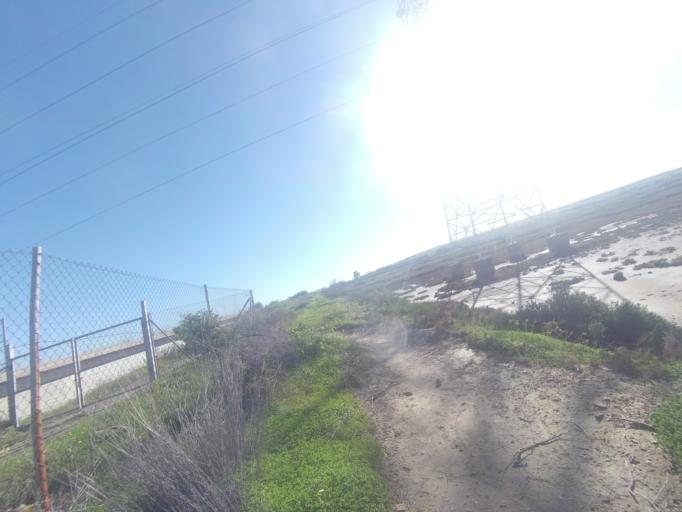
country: ES
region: Andalusia
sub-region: Provincia de Huelva
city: Huelva
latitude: 37.2588
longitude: -6.9185
